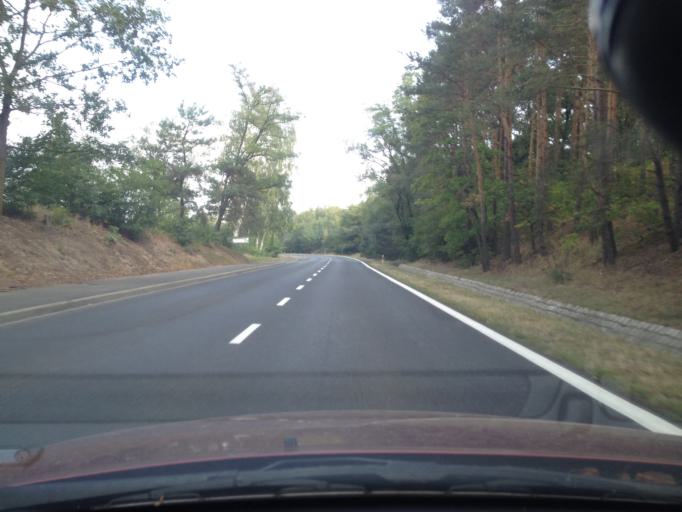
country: PL
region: Lubusz
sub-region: Powiat zaganski
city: Szprotawa
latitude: 51.4340
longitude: 15.6014
